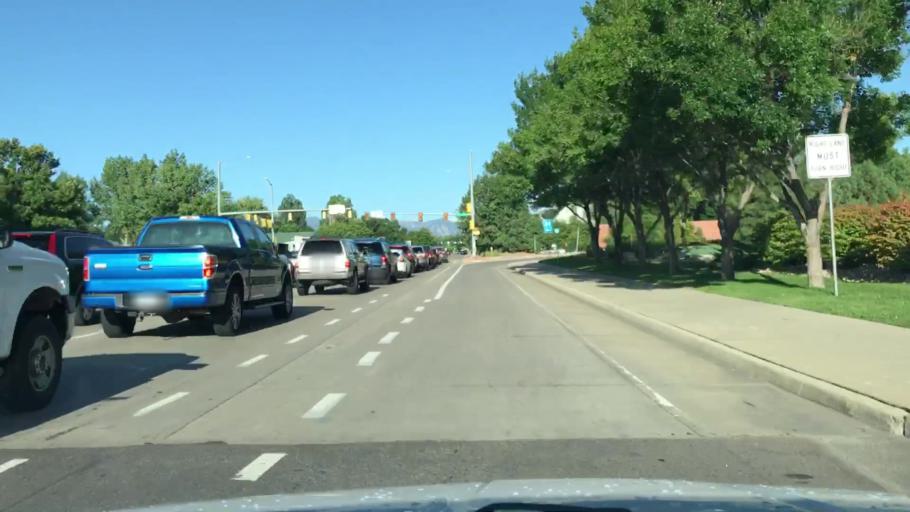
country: US
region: Colorado
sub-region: Boulder County
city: Lafayette
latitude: 39.9872
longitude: -105.0971
